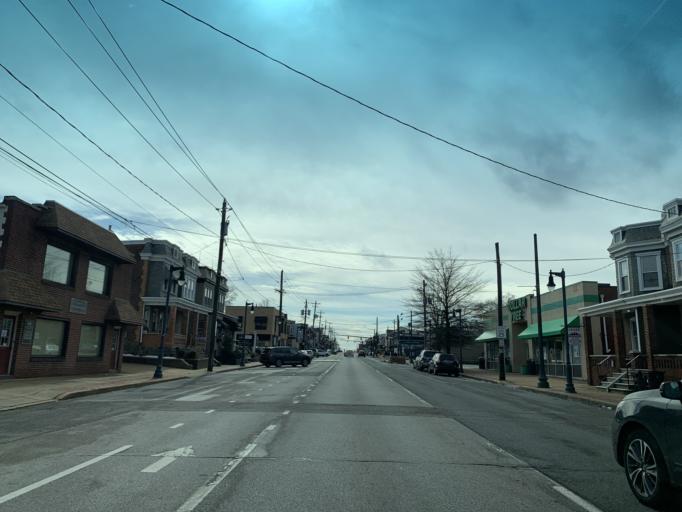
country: US
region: Delaware
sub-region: New Castle County
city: Wilmington
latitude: 39.7535
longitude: -75.5701
